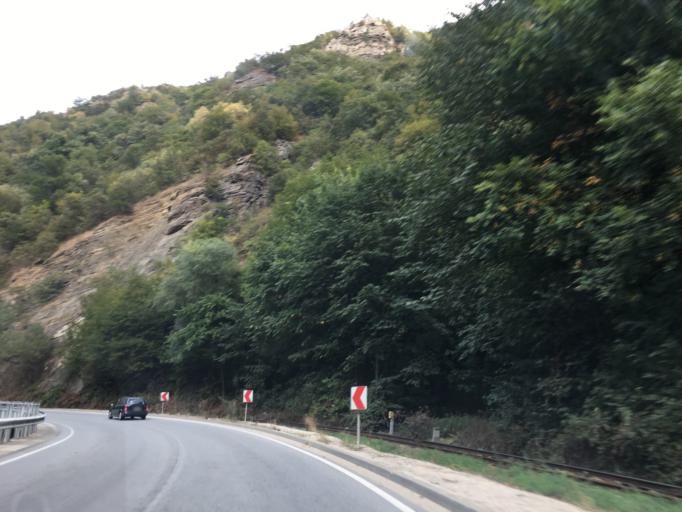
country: BG
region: Pazardzhik
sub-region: Obshtina Septemvri
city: Septemvri
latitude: 42.1184
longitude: 24.1188
